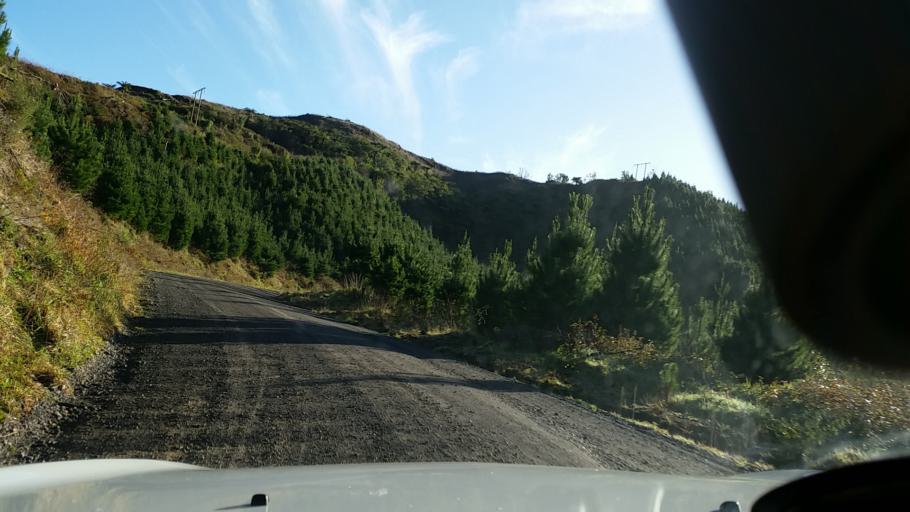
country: NZ
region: Bay of Plenty
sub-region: Kawerau District
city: Kawerau
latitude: -38.0348
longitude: 176.5519
